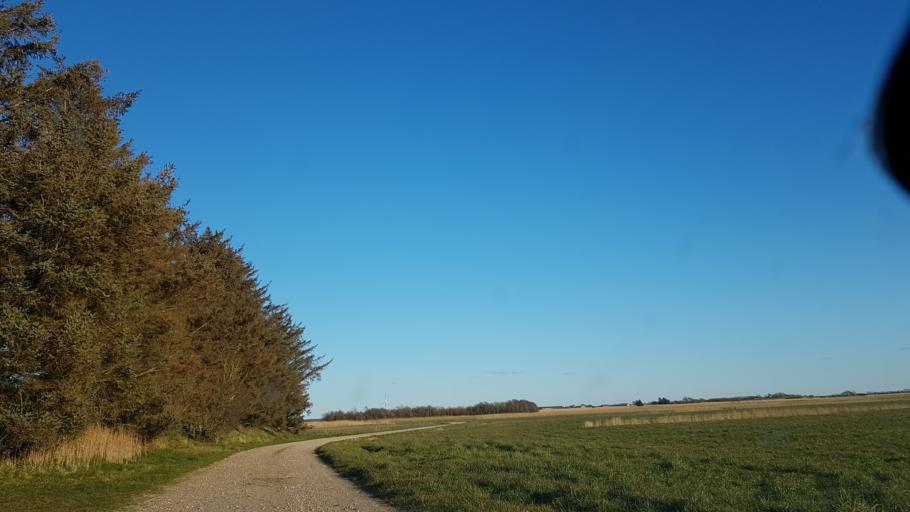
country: DK
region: South Denmark
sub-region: Esbjerg Kommune
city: Bramming
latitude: 55.4173
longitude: 8.6459
